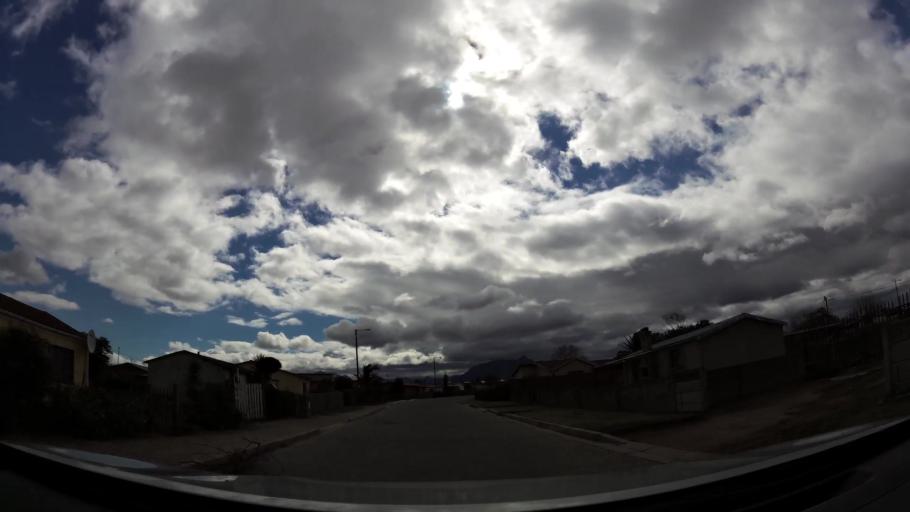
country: ZA
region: Western Cape
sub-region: Eden District Municipality
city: George
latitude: -34.0240
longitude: 22.4644
